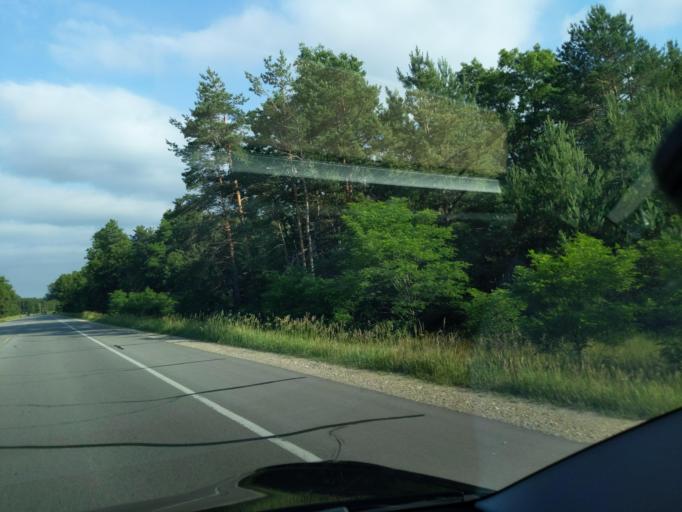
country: US
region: Michigan
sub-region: Muskegon County
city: Lakewood Club
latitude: 43.3902
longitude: -86.2955
